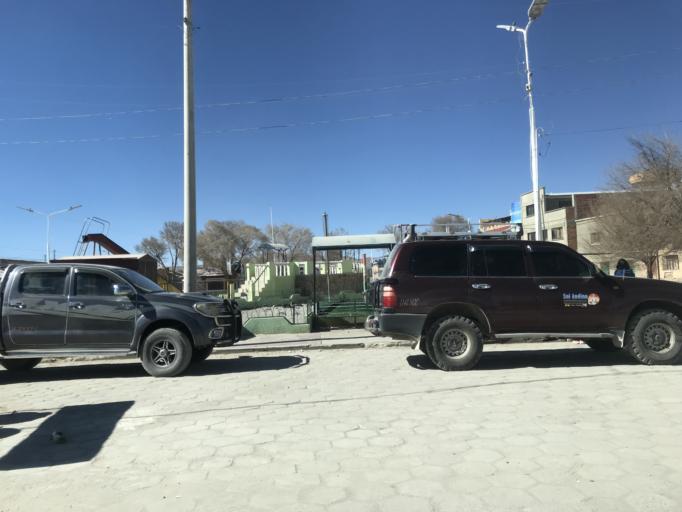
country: BO
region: Potosi
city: Uyuni
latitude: -20.4661
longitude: -66.8239
